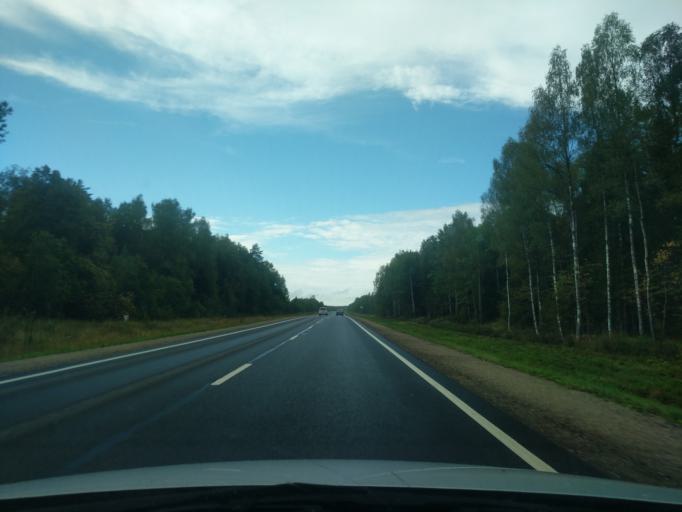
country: RU
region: Kostroma
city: Ostrovskoye
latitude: 57.8141
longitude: 42.0079
